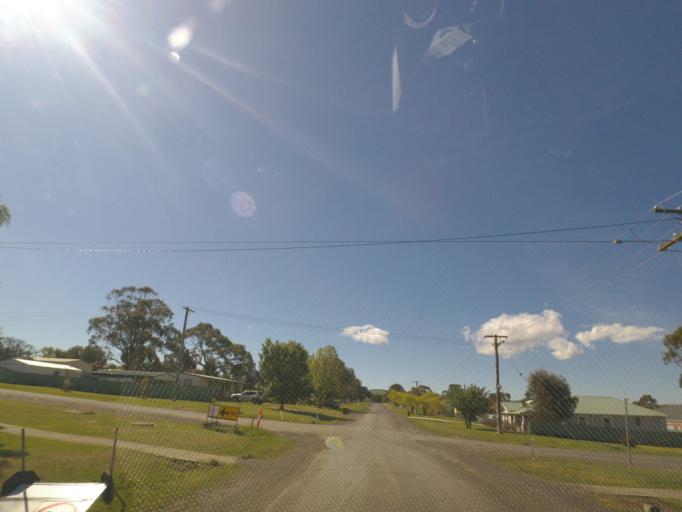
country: AU
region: Victoria
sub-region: Moorabool
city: Bacchus Marsh
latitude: -37.6039
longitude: 144.2334
